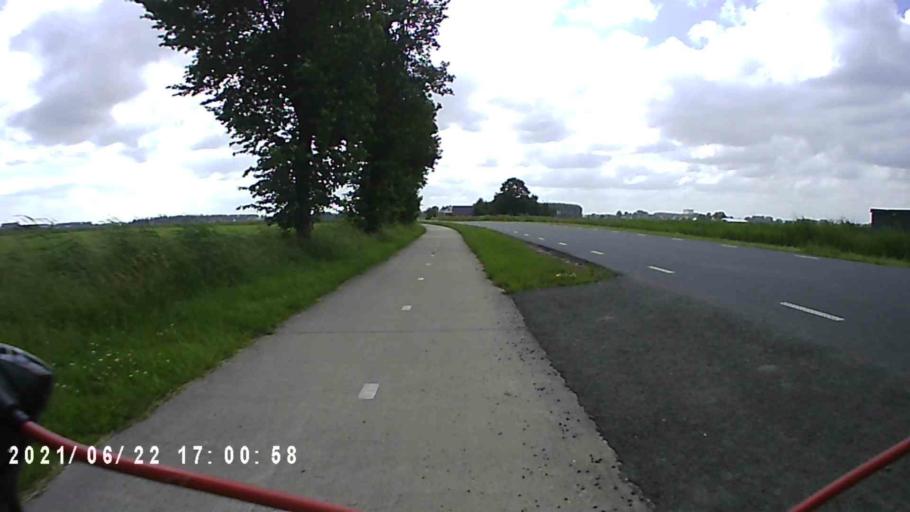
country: NL
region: Groningen
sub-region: Gemeente Bedum
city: Bedum
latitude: 53.3025
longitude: 6.6312
